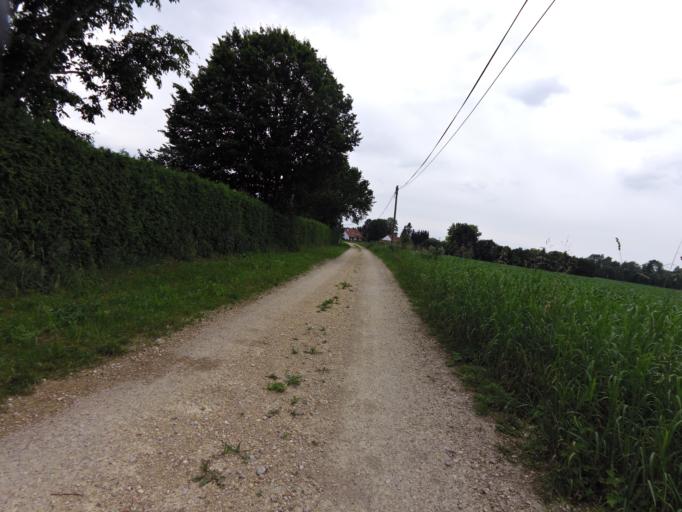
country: DE
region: Bavaria
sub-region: Lower Bavaria
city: Bruckberg
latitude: 48.4908
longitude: 12.0056
